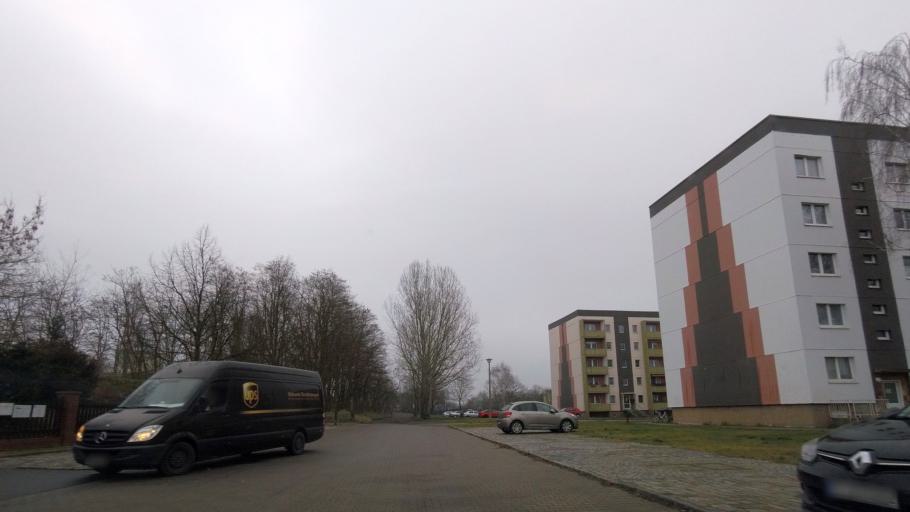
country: DE
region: Brandenburg
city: Juterbog
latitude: 52.0048
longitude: 13.0709
